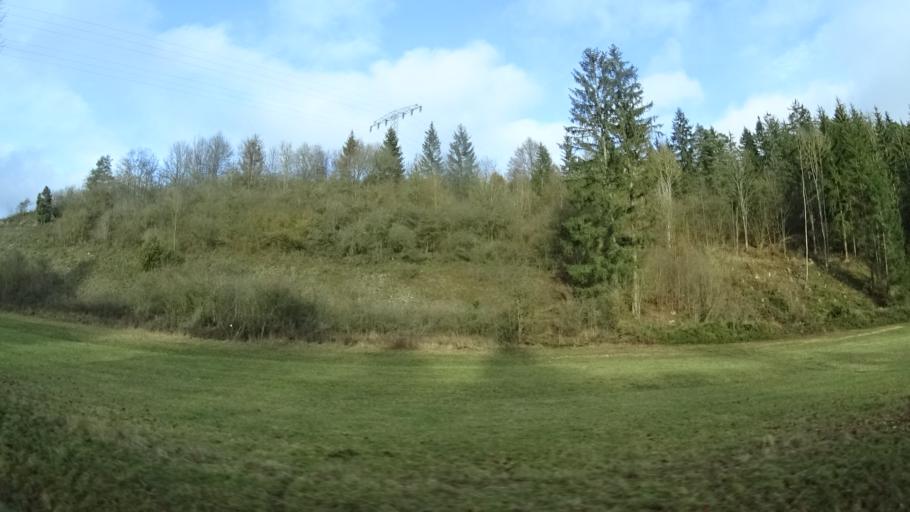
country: DE
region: Thuringia
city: Utendorf
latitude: 50.6020
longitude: 10.4421
